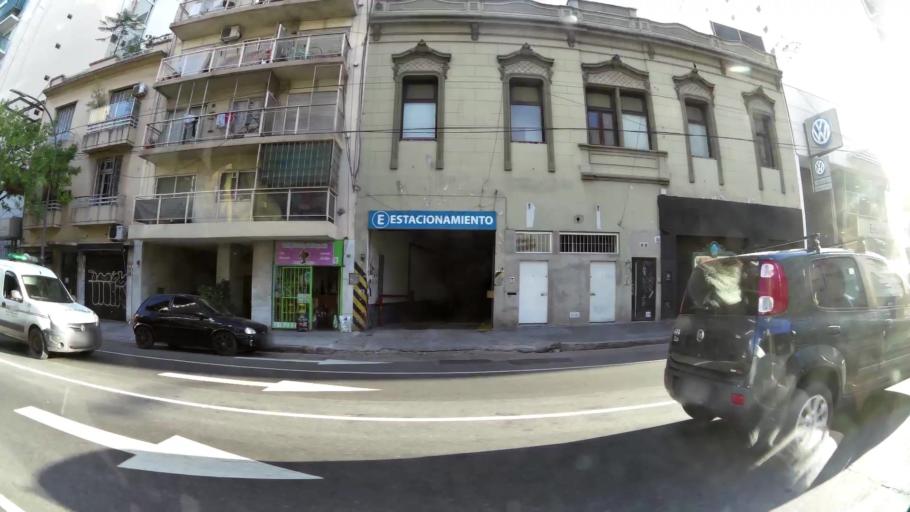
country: AR
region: Buenos Aires F.D.
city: Retiro
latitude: -34.5987
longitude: -58.4093
